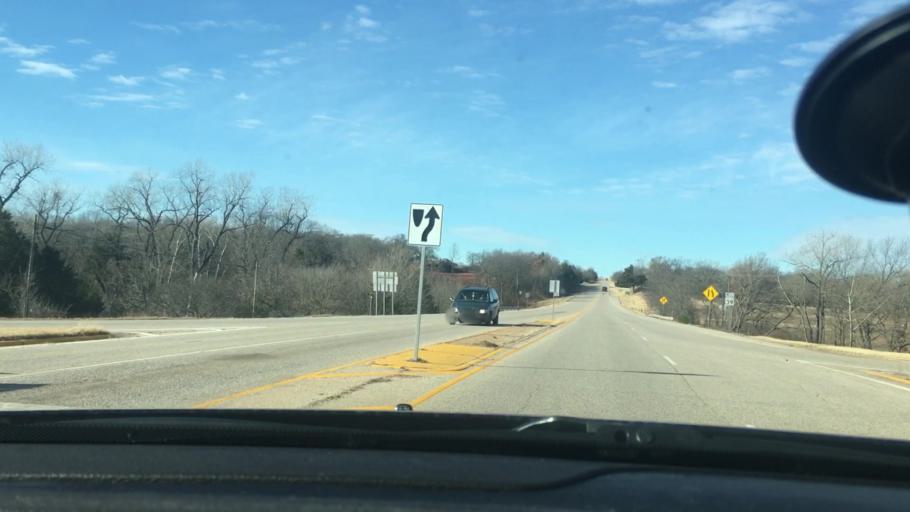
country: US
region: Oklahoma
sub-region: Seminole County
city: Konawa
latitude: 34.9860
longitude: -96.9302
